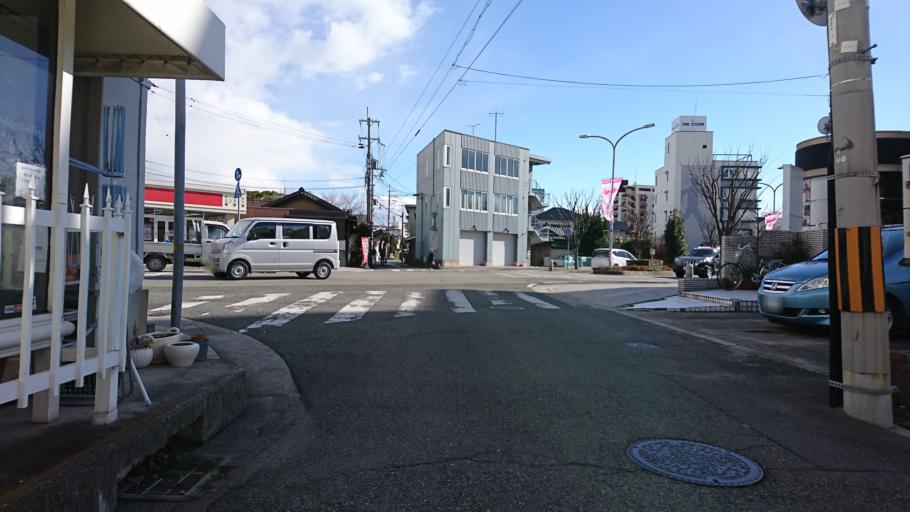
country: JP
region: Hyogo
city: Kakogawacho-honmachi
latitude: 34.7636
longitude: 134.8407
